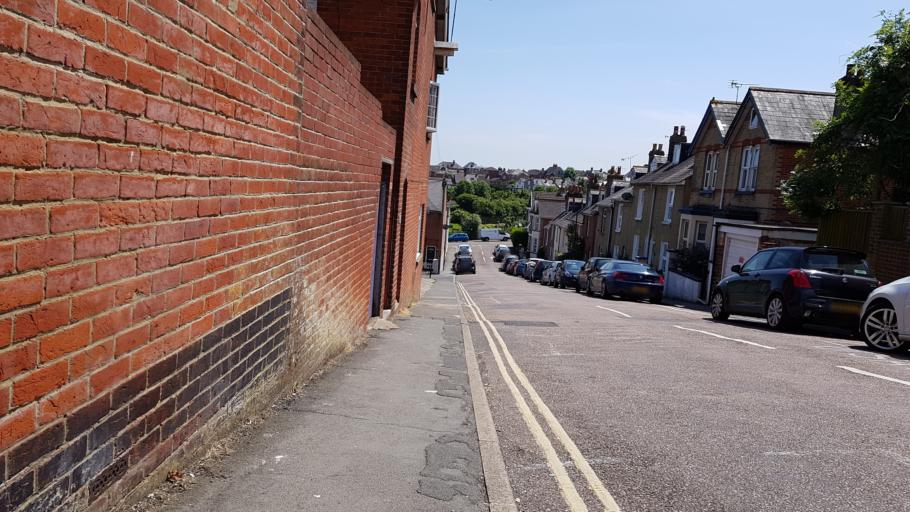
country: GB
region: England
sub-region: Isle of Wight
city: Cowes
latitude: 50.7594
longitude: -1.3049
